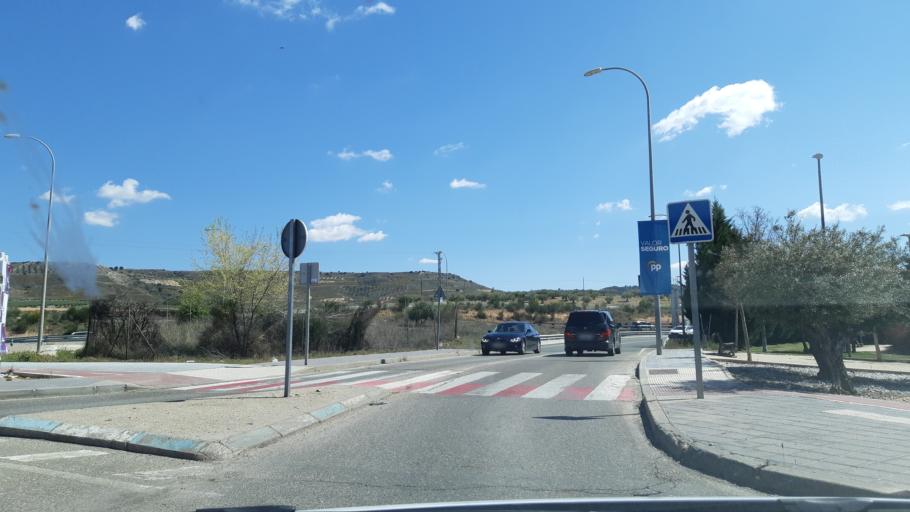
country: ES
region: Castille-La Mancha
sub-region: Provincia de Guadalajara
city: Guadalajara
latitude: 40.6305
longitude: -3.1496
